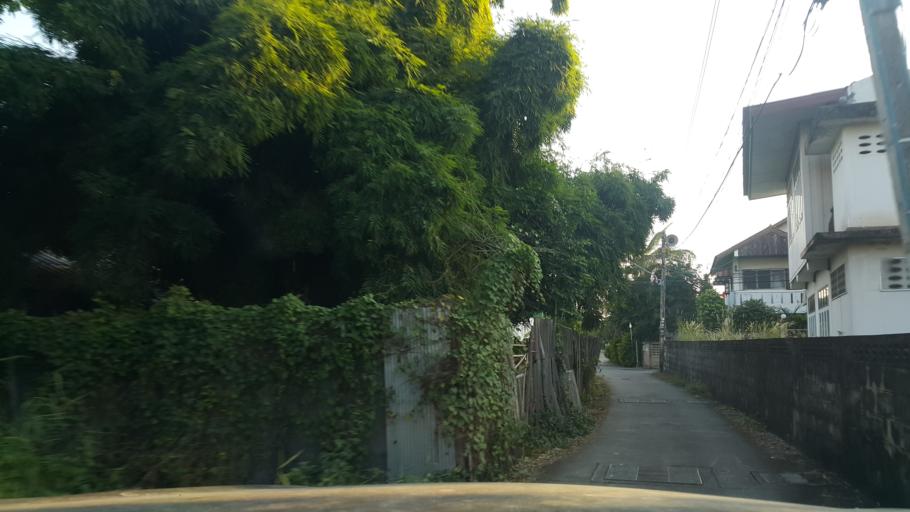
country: TH
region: Lampang
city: Lampang
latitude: 18.2771
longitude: 99.4683
